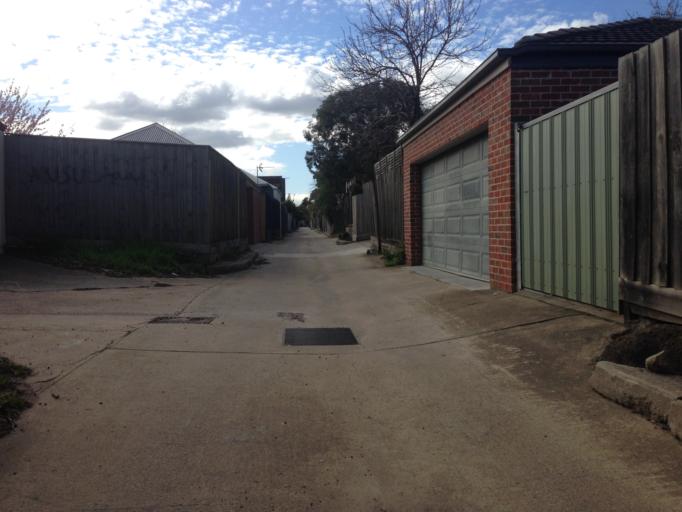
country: AU
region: Victoria
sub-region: Darebin
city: Northcote
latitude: -37.7727
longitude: 145.0082
